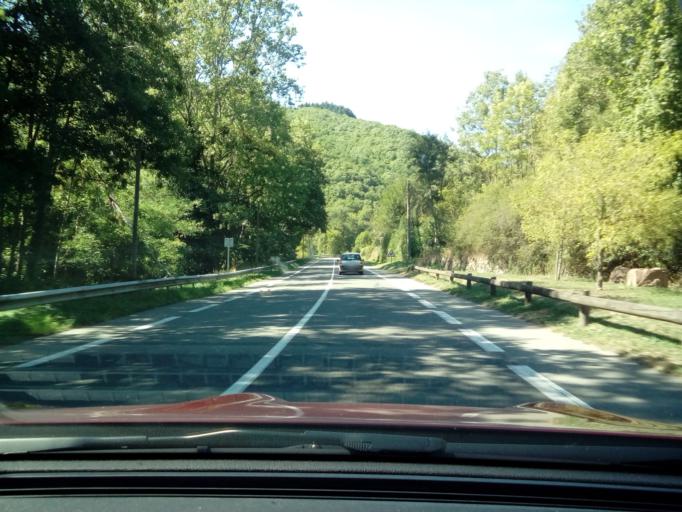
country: FR
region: Rhone-Alpes
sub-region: Departement du Rhone
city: Tarare
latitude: 45.9258
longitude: 4.4474
